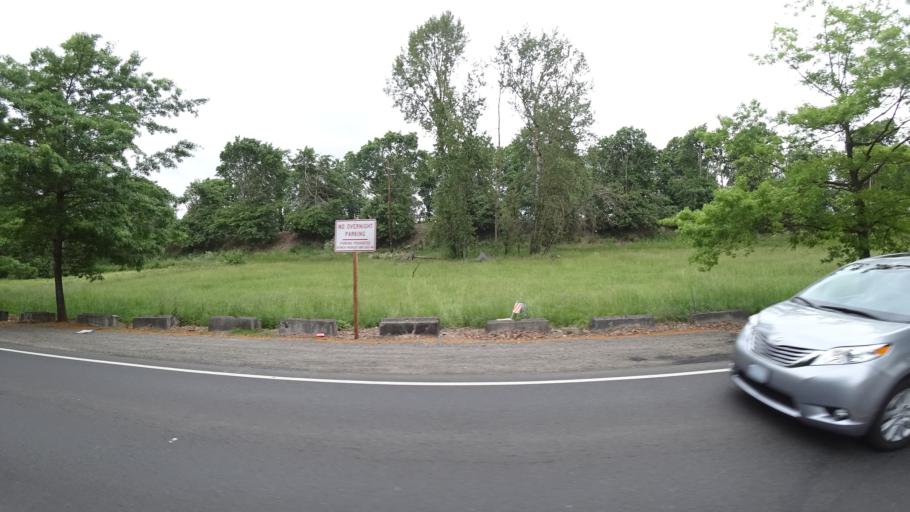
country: US
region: Washington
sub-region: Clark County
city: Vancouver
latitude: 45.5985
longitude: -122.6751
